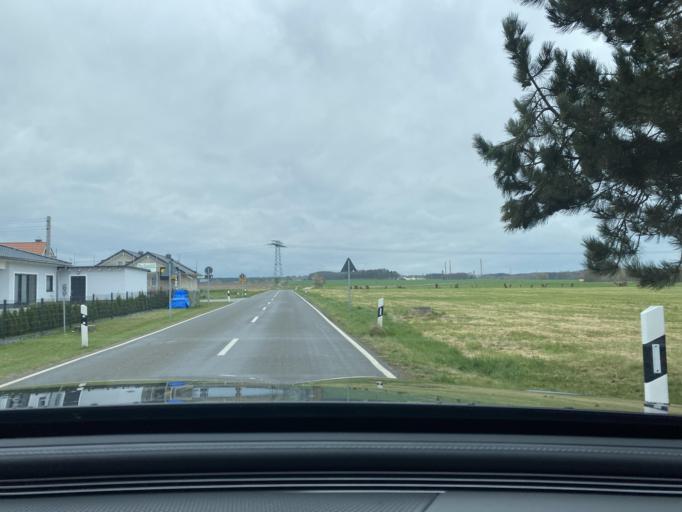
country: DE
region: Saxony
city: Neschwitz
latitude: 51.2674
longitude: 14.3259
